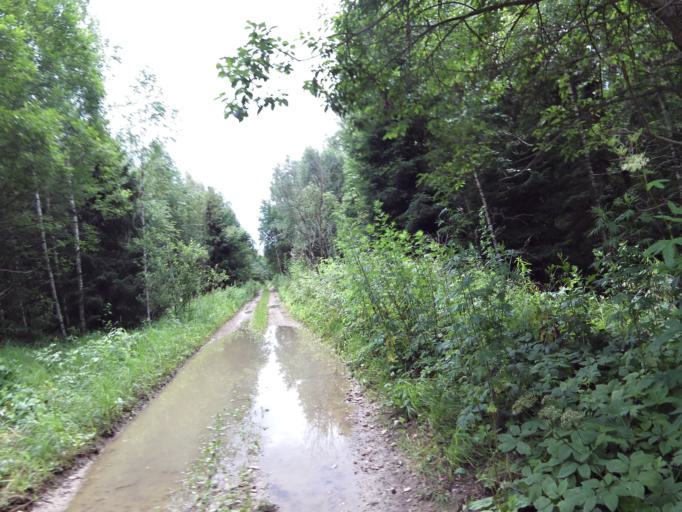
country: RU
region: Moskovskaya
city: Popovo
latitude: 54.9697
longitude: 37.6971
